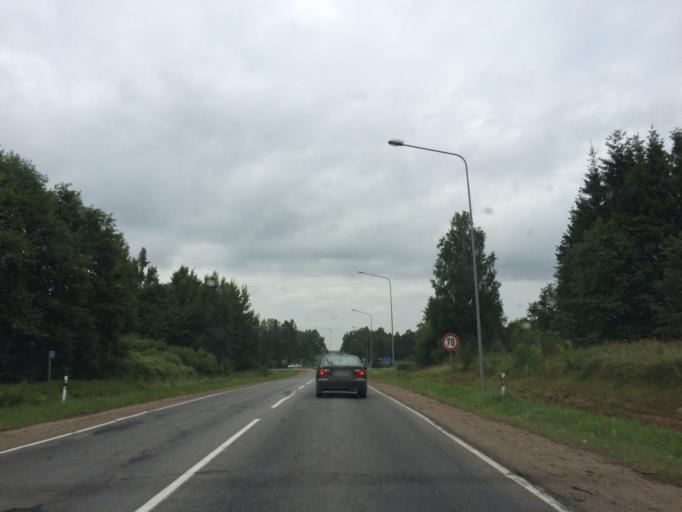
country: LV
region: Rezekne
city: Rezekne
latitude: 56.5426
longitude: 27.3529
